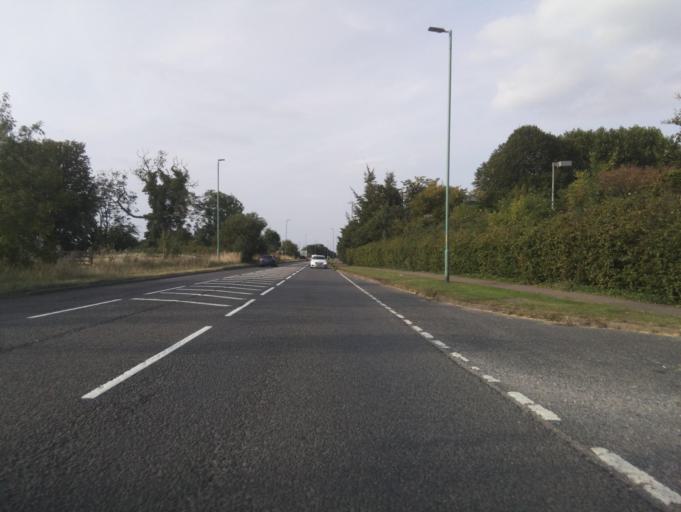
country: GB
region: England
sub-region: Gloucestershire
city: Gotherington
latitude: 51.9432
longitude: -2.0725
